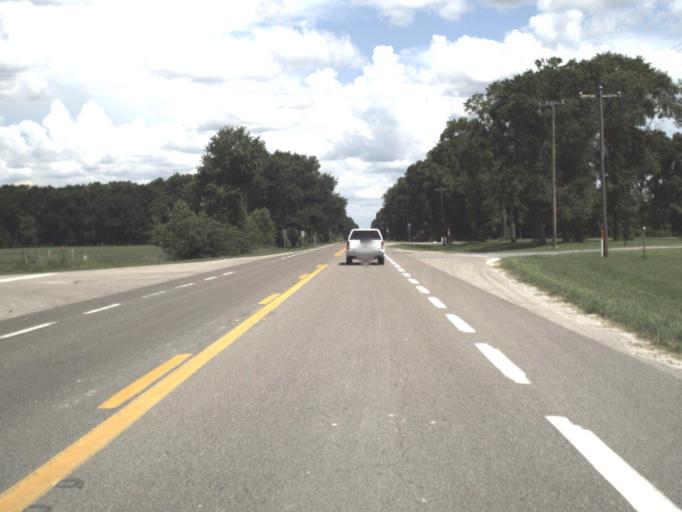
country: US
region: Florida
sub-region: Lafayette County
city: Mayo
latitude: 29.9755
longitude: -82.9878
